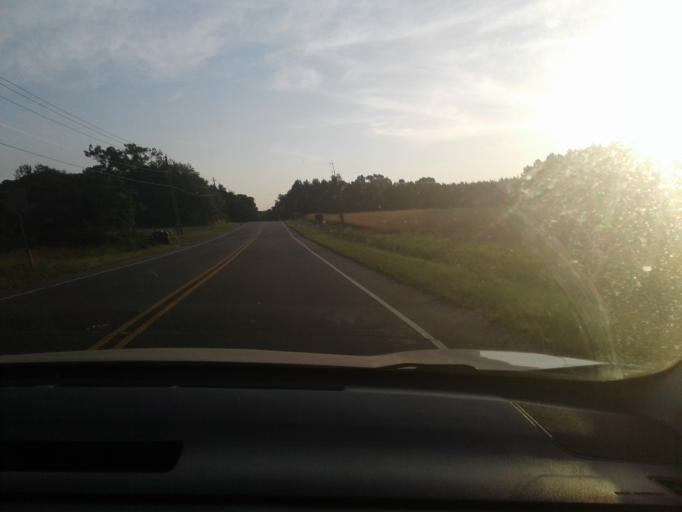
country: US
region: North Carolina
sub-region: Wake County
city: Fuquay-Varina
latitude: 35.5509
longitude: -78.8130
